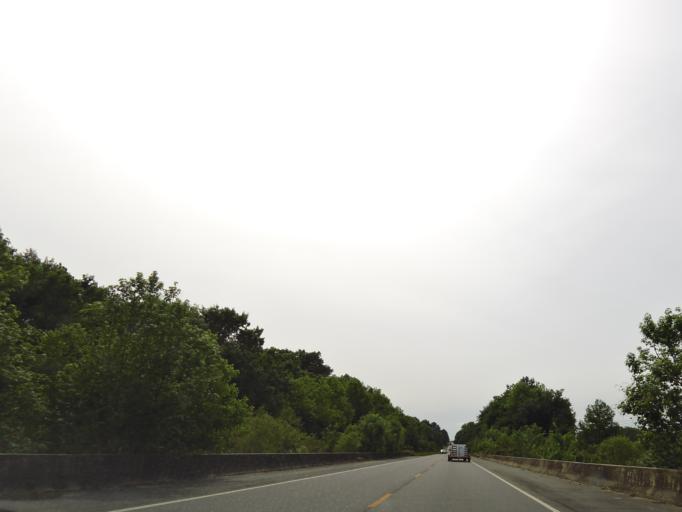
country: US
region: Georgia
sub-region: Houston County
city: Robins Air Force Base
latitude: 32.5431
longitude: -83.5488
